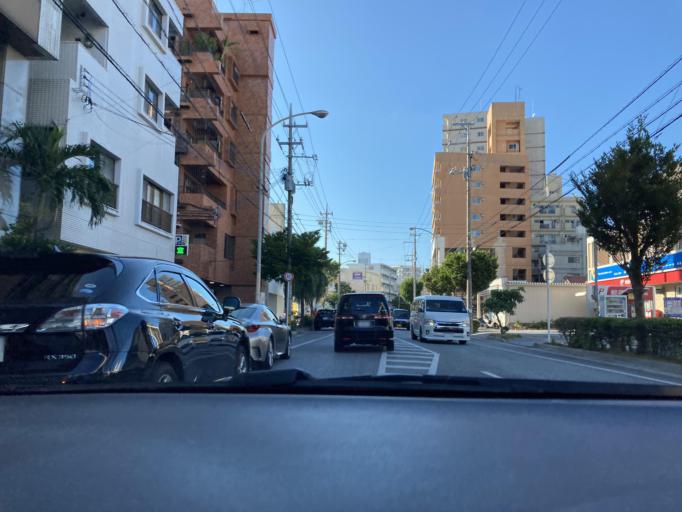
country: JP
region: Okinawa
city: Naha-shi
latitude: 26.2233
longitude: 127.6868
